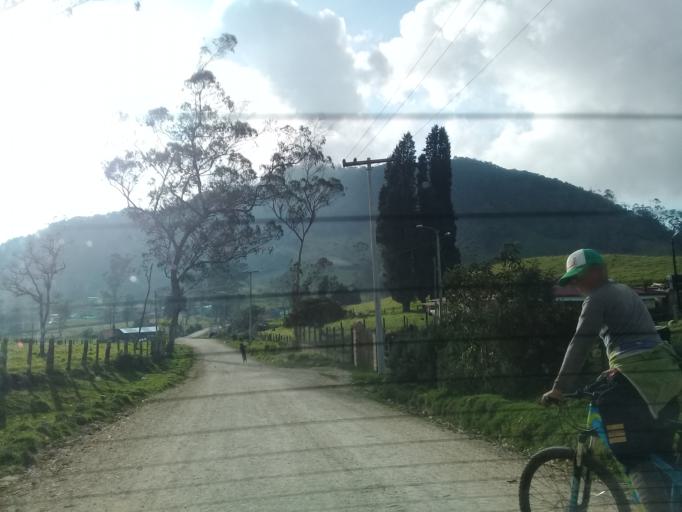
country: CO
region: Cundinamarca
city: Sibate
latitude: 4.4276
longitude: -74.2891
